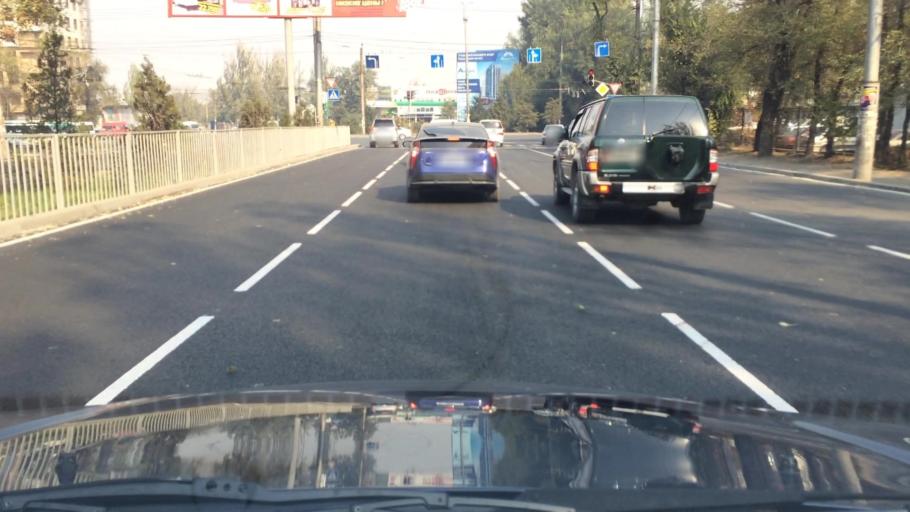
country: KG
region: Chuy
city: Lebedinovka
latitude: 42.8742
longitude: 74.6373
